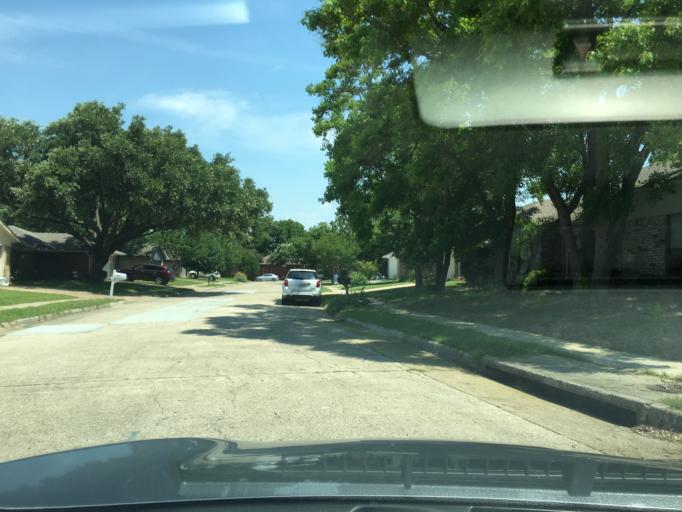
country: US
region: Texas
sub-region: Dallas County
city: Richardson
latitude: 32.9631
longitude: -96.6974
